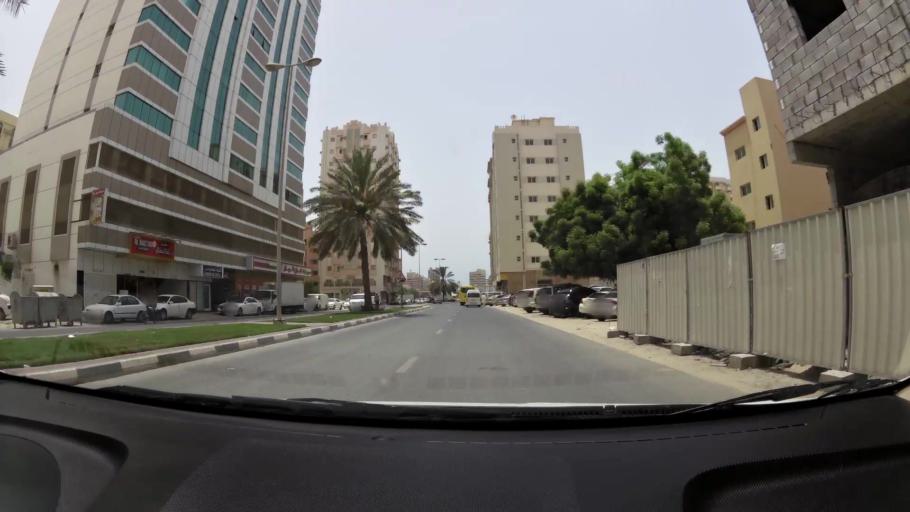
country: AE
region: Ash Shariqah
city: Sharjah
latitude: 25.3550
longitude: 55.3935
